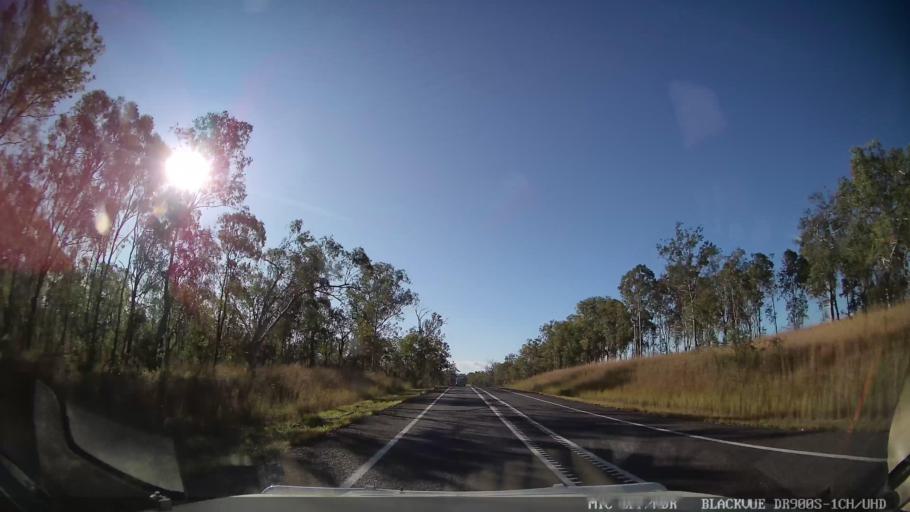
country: AU
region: Queensland
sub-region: Bundaberg
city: Sharon
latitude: -24.8371
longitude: 151.7102
